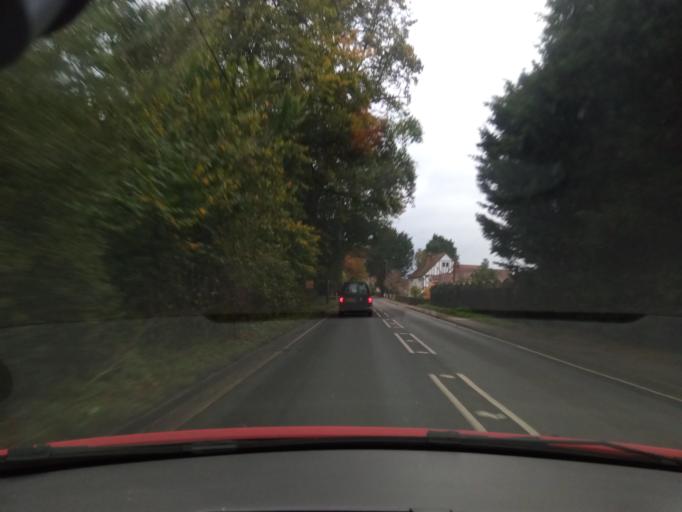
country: GB
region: England
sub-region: Essex
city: Great Yeldham
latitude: 52.0040
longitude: 0.5690
